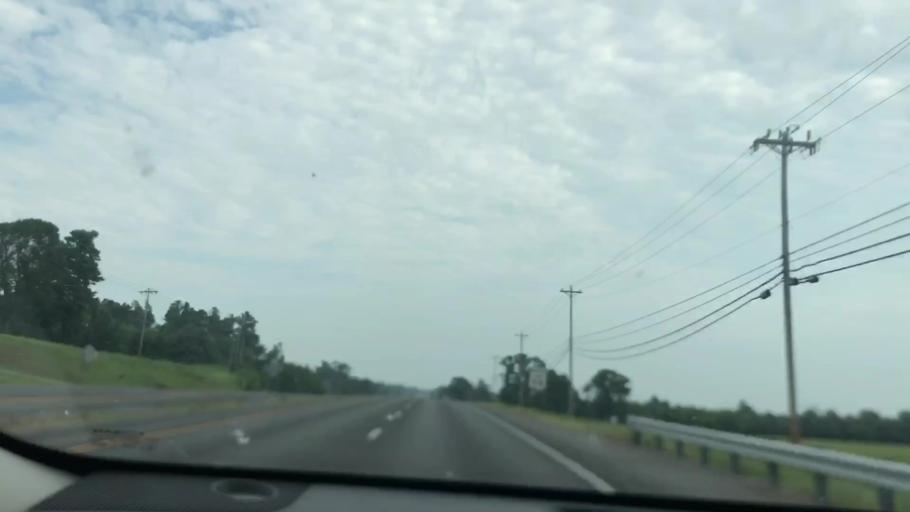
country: US
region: Kentucky
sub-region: Calloway County
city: Murray
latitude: 36.6474
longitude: -88.3077
